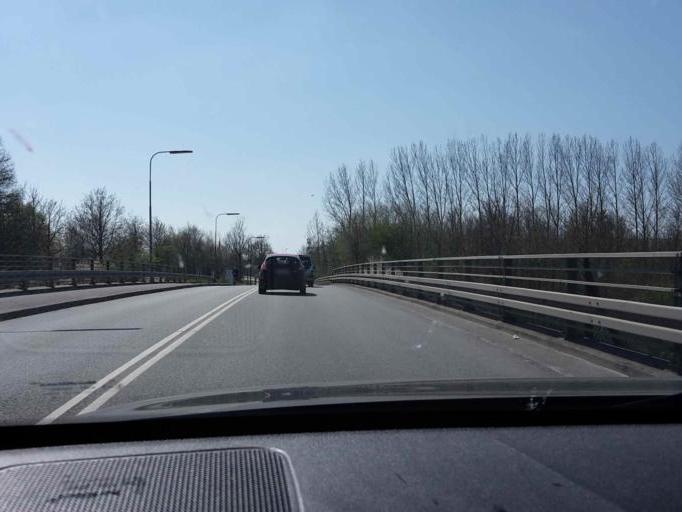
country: DK
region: South Denmark
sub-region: Odense Kommune
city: Bellinge
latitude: 55.3641
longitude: 10.3266
